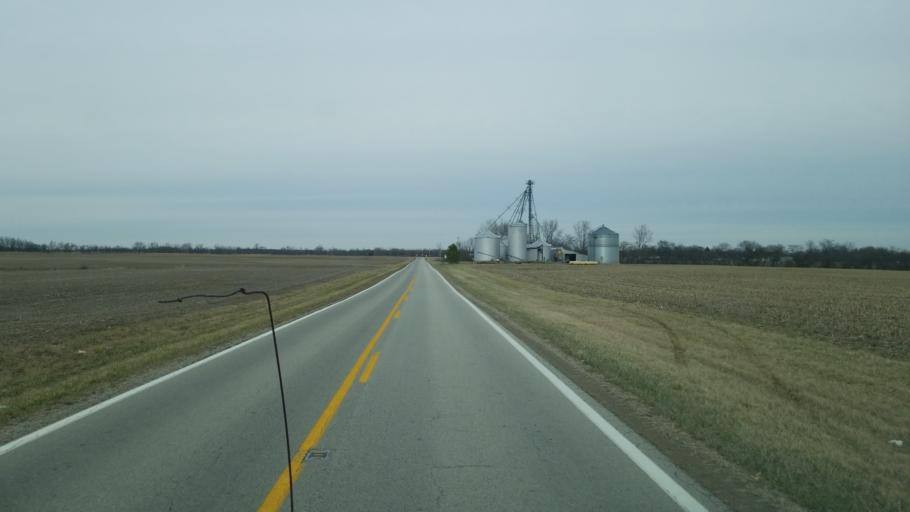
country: US
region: Ohio
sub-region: Ross County
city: Frankfort
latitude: 39.4977
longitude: -83.1659
